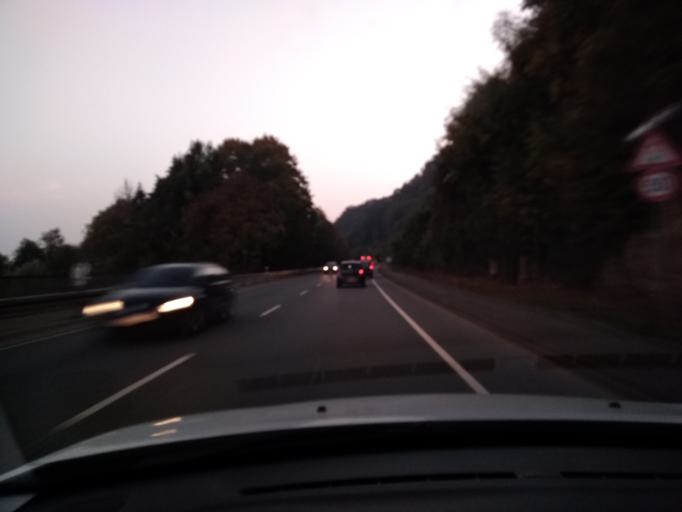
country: FR
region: Lorraine
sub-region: Departement de la Moselle
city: Alsting
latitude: 49.2055
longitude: 7.0180
